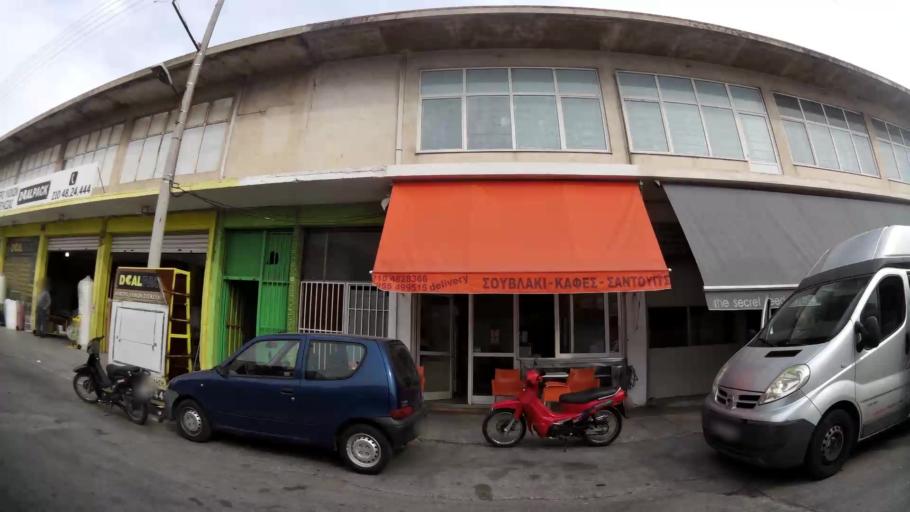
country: GR
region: Attica
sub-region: Nomarchia Athinas
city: Tavros
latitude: 37.9601
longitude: 23.6851
